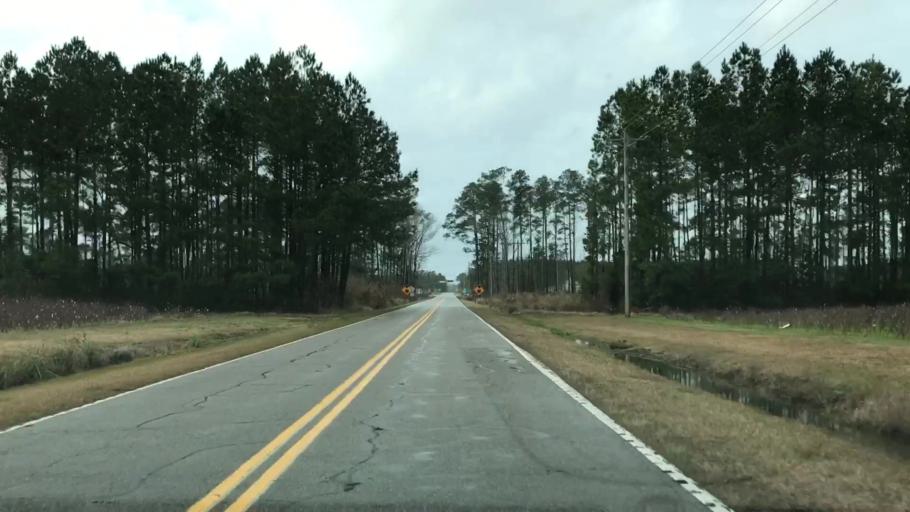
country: US
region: South Carolina
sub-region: Florence County
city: Johnsonville
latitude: 33.6694
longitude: -79.3141
